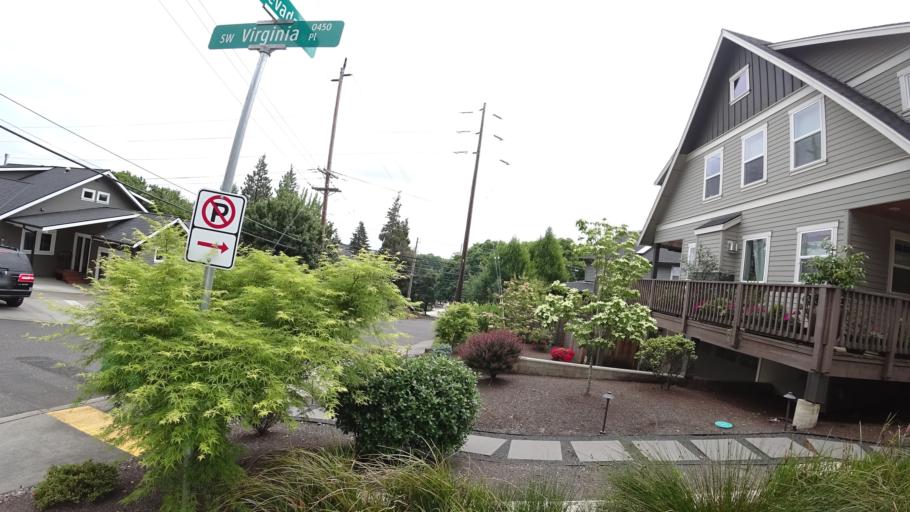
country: US
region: Oregon
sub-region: Clackamas County
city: Milwaukie
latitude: 45.4729
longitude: -122.6744
